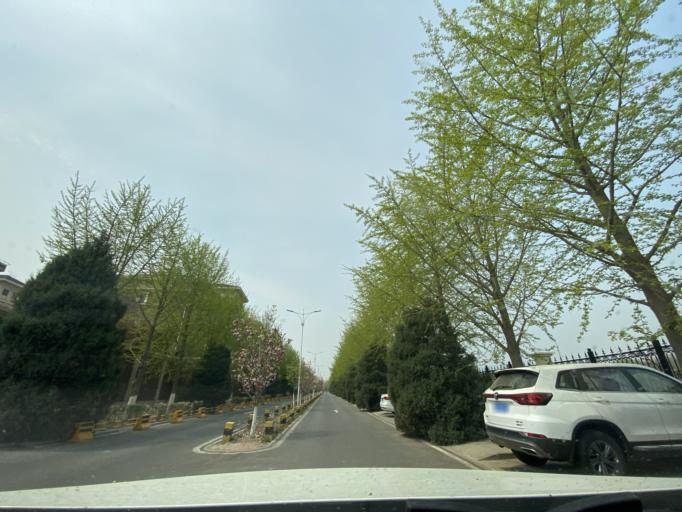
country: CN
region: Beijing
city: Sijiqing
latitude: 39.9429
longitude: 116.2450
